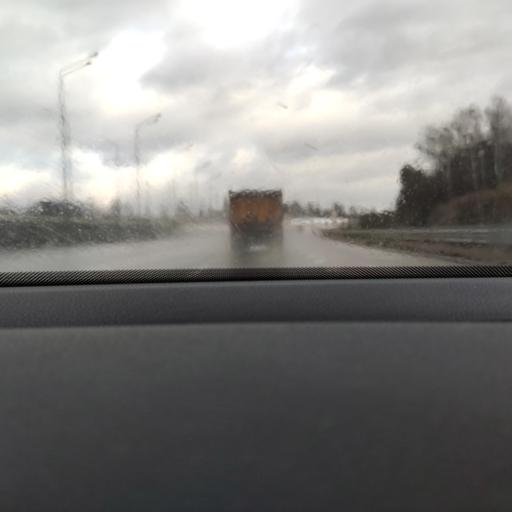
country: RU
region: Moskovskaya
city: Pavlovskaya Sloboda
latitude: 55.7870
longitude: 37.1222
